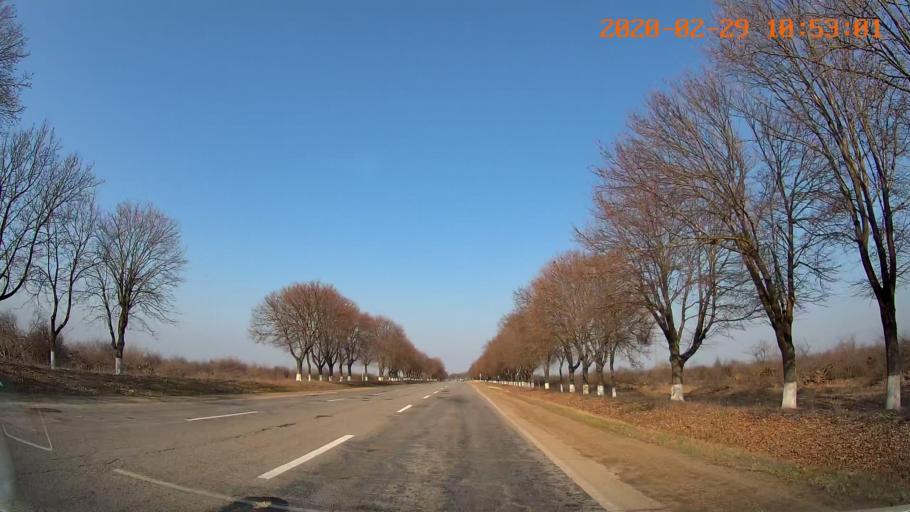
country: MD
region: Telenesti
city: Grigoriopol
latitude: 47.1112
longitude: 29.3422
